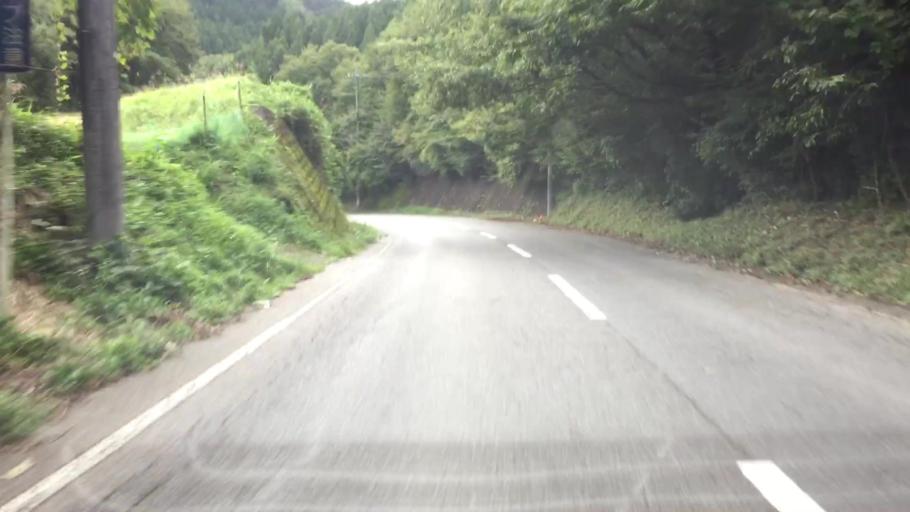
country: JP
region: Tochigi
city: Imaichi
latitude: 36.7572
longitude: 139.6621
